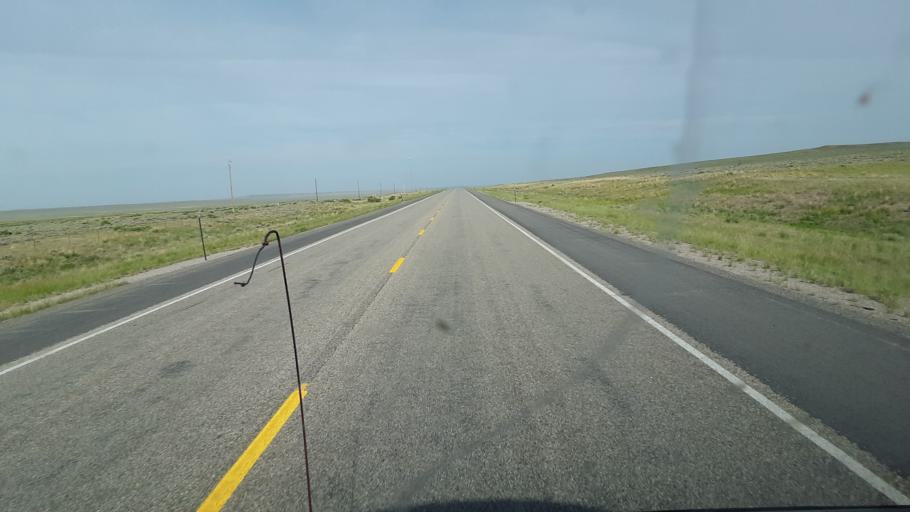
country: US
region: Wyoming
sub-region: Fremont County
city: Riverton
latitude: 43.1398
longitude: -107.5952
